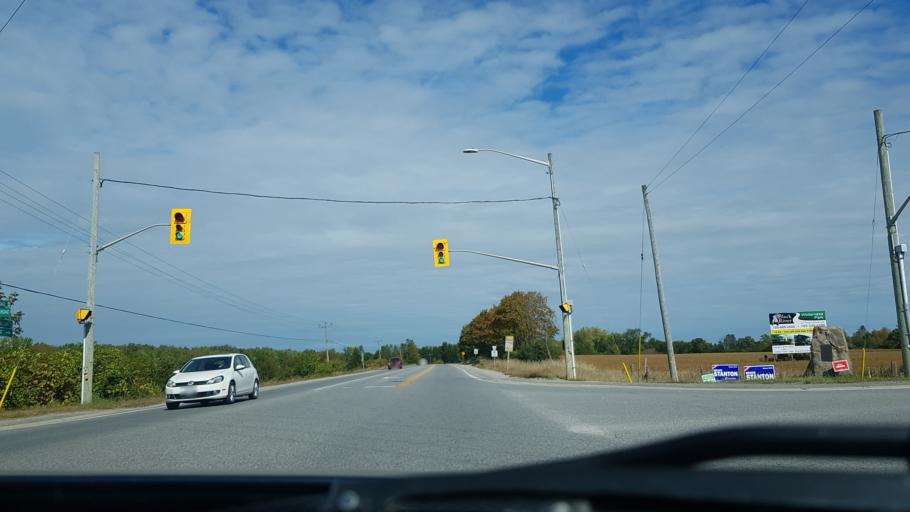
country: CA
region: Ontario
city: Orillia
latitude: 44.6247
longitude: -79.3519
